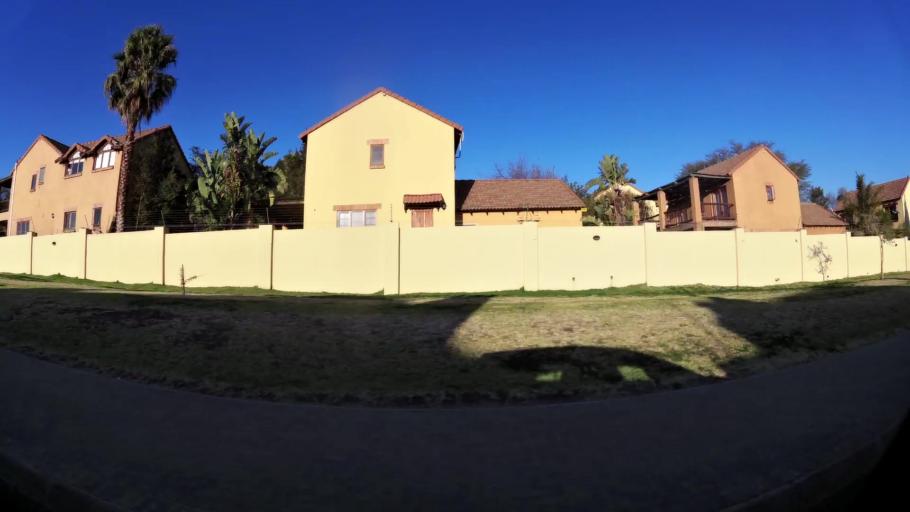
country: ZA
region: Gauteng
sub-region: City of Johannesburg Metropolitan Municipality
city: Midrand
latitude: -25.9806
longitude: 28.1121
